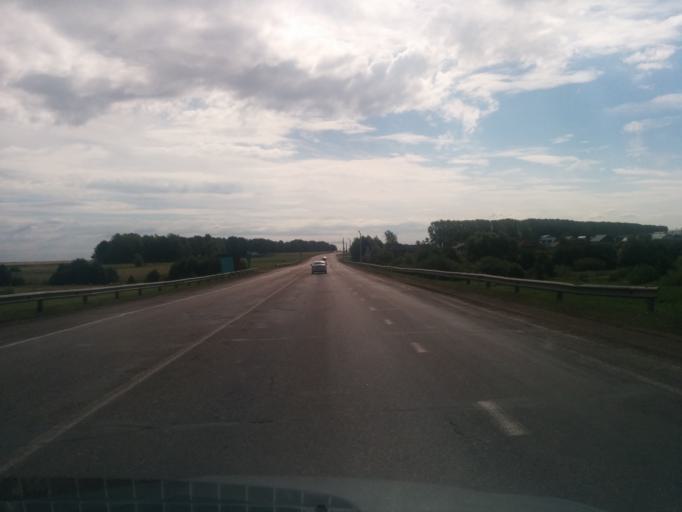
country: RU
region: Bashkortostan
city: Kabakovo
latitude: 54.4666
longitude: 55.9548
